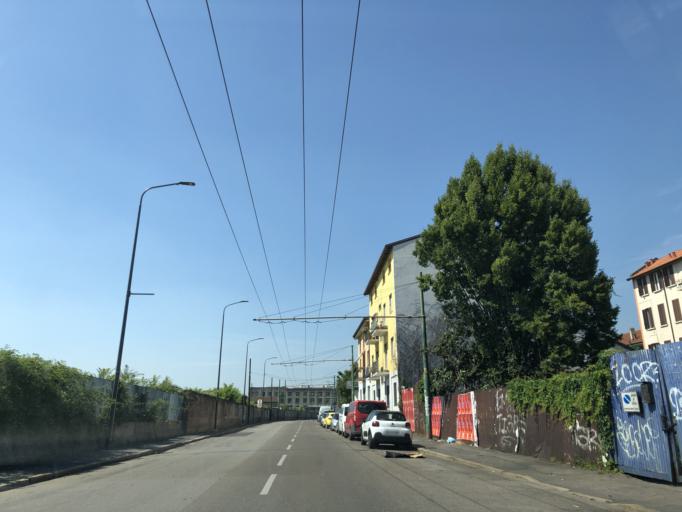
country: IT
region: Lombardy
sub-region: Citta metropolitana di Milano
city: Novate Milanese
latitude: 45.5039
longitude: 9.1608
